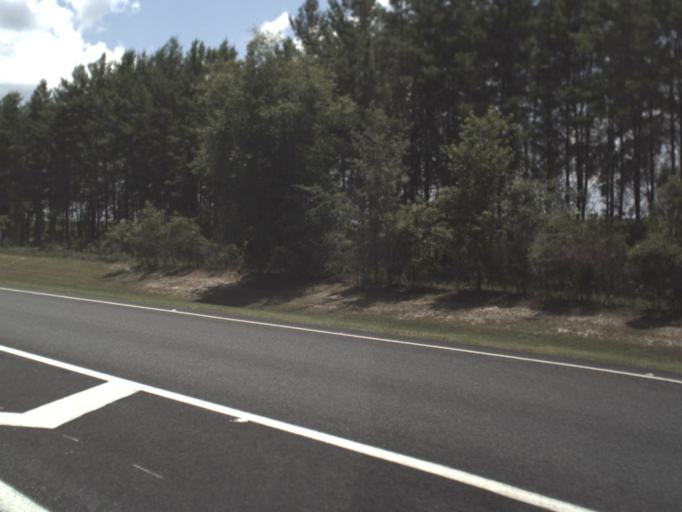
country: US
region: Florida
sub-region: Madison County
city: Madison
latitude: 30.3716
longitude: -83.2630
